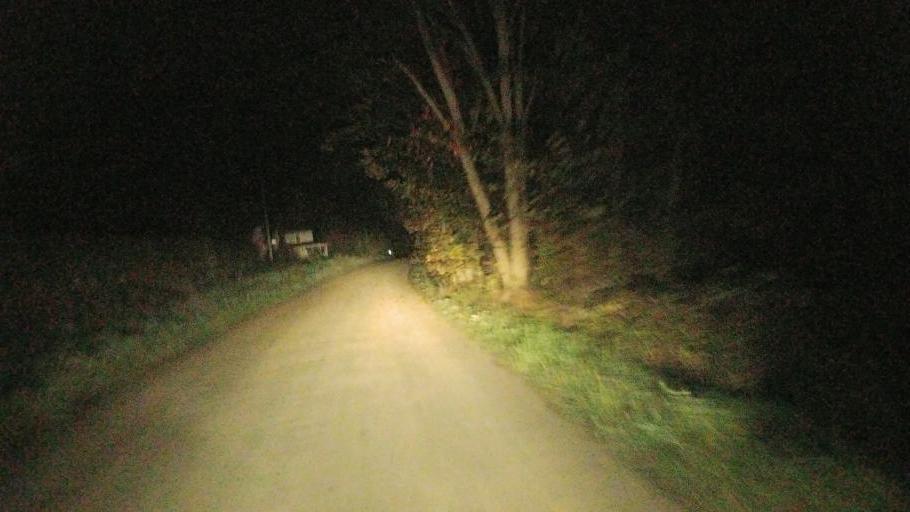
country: US
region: Ohio
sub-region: Knox County
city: Fredericktown
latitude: 40.5551
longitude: -82.6374
